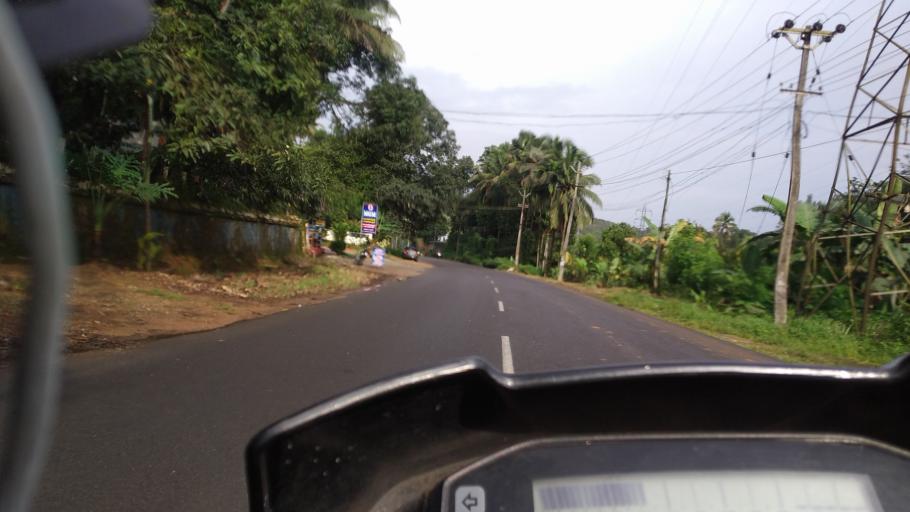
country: IN
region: Kerala
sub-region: Ernakulam
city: Kotamangalam
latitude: 10.0524
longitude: 76.7032
